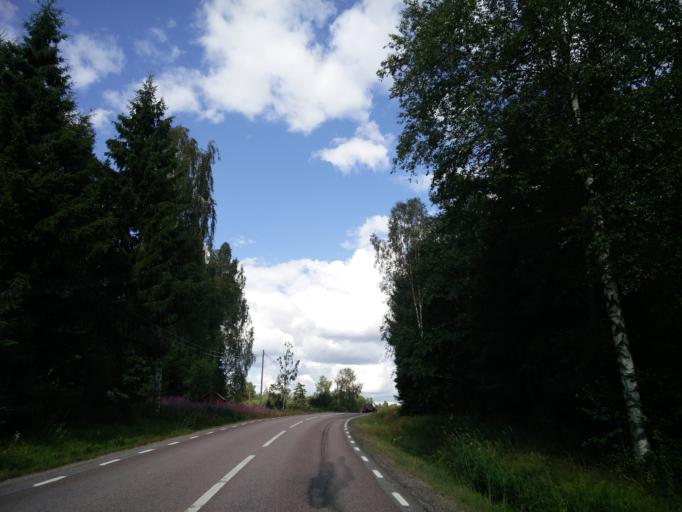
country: SE
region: Vaermland
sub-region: Sunne Kommun
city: Sunne
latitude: 59.6687
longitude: 12.9853
